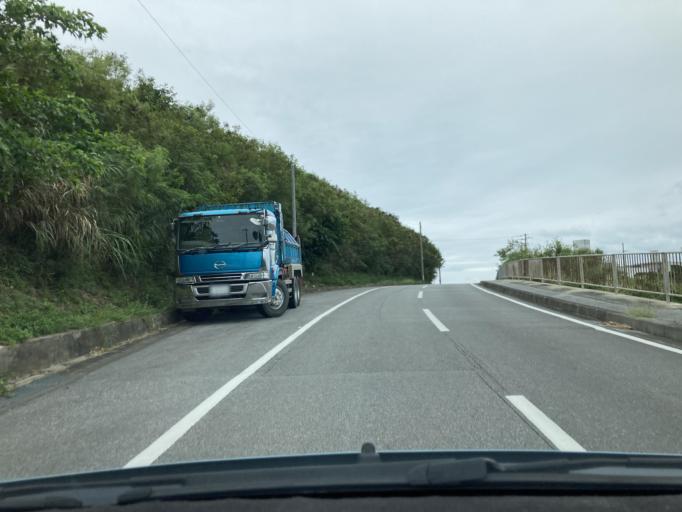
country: JP
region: Okinawa
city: Tomigusuku
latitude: 26.1569
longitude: 127.7011
